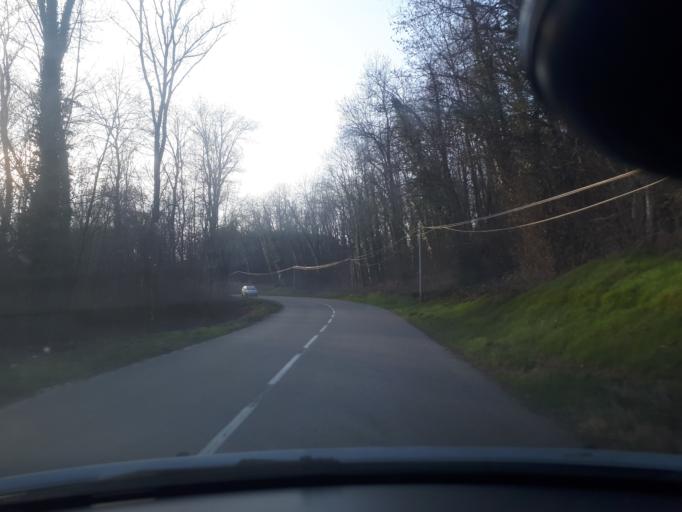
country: FR
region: Rhone-Alpes
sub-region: Departement de l'Isere
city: Sermerieu
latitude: 45.6695
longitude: 5.4353
